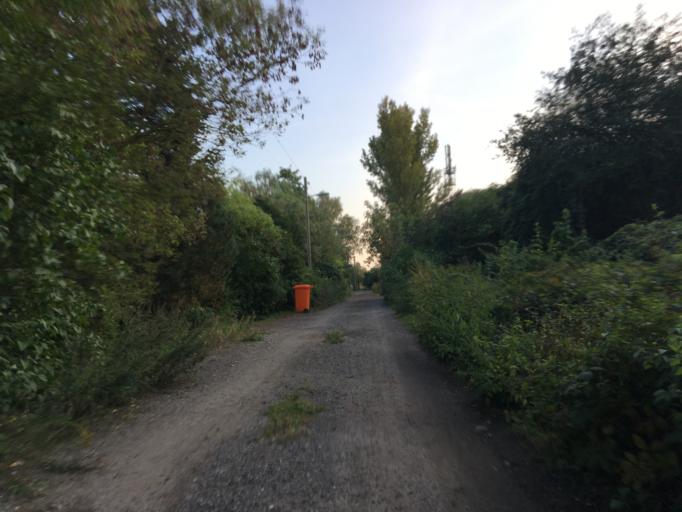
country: DE
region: Berlin
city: Biesdorf
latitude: 52.4893
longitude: 13.5520
